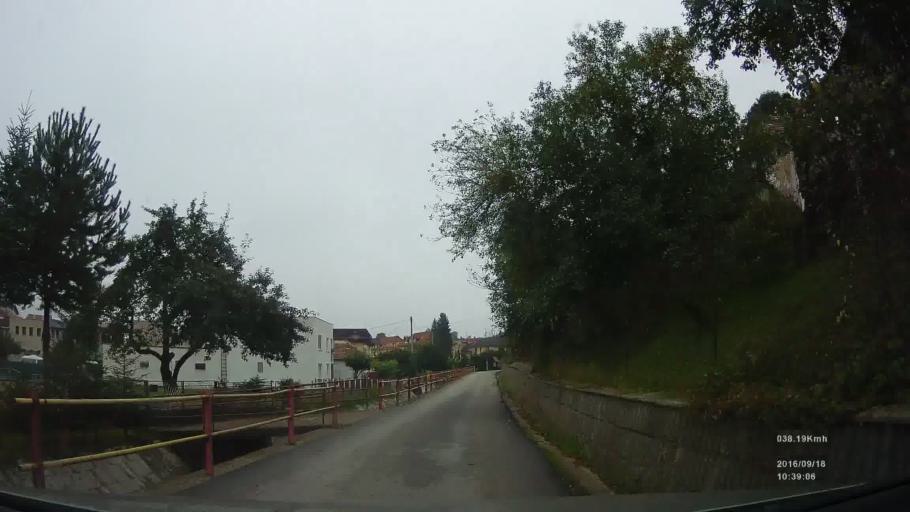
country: SK
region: Kosicky
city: Spisska Nova Ves
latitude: 48.9500
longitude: 20.6201
